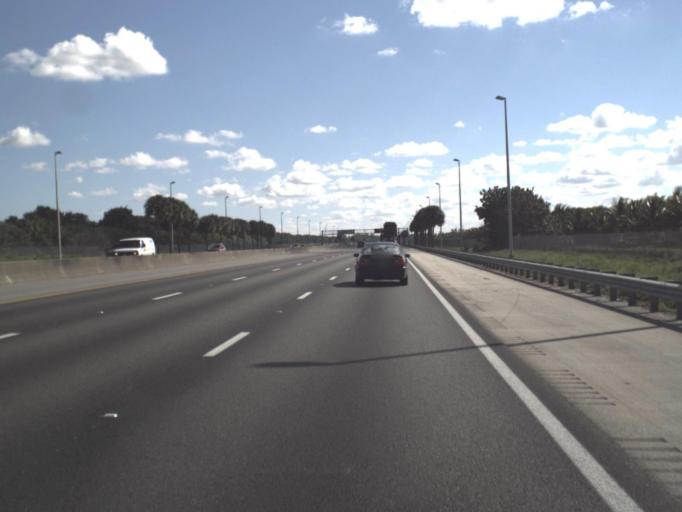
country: US
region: Florida
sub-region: Palm Beach County
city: Villages of Oriole
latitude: 26.5039
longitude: -80.1727
